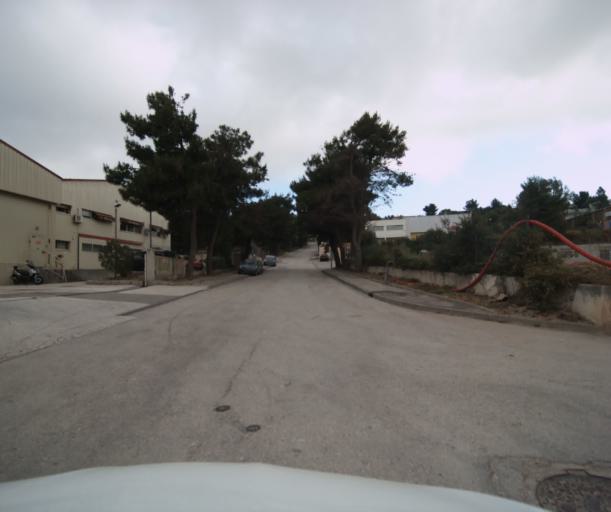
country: FR
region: Provence-Alpes-Cote d'Azur
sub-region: Departement du Var
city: La Seyne-sur-Mer
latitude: 43.1171
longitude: 5.8727
